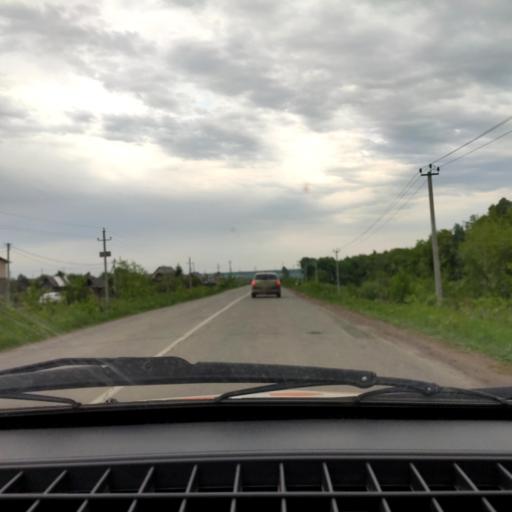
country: RU
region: Bashkortostan
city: Avdon
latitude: 54.5783
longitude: 55.7520
